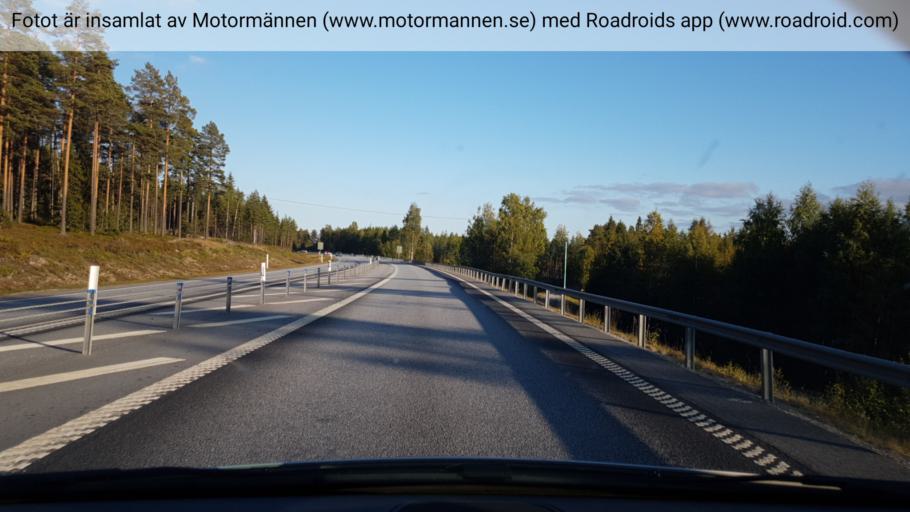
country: SE
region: Vaesterbotten
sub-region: Vannas Kommun
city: Vannasby
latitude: 63.8894
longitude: 19.9973
